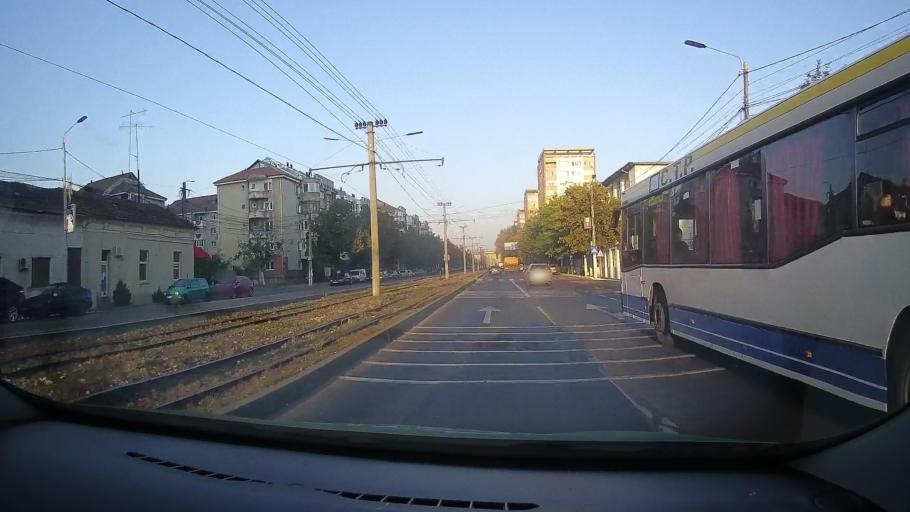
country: RO
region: Arad
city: Arad
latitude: 46.1817
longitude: 21.3303
